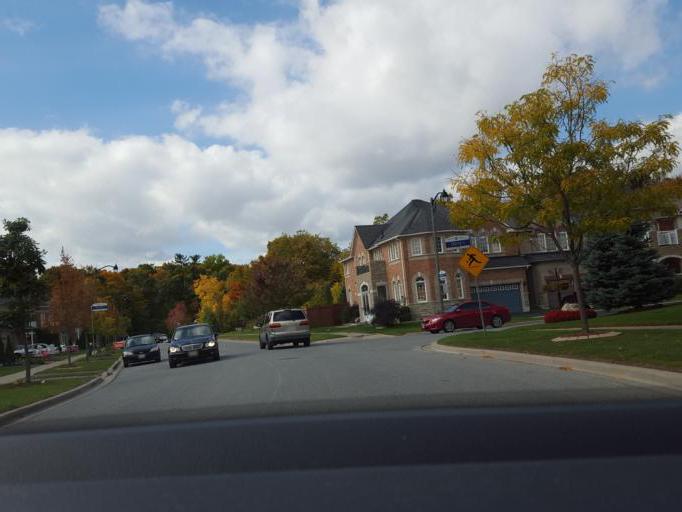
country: CA
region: Ontario
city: Markham
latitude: 43.8345
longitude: -79.2279
